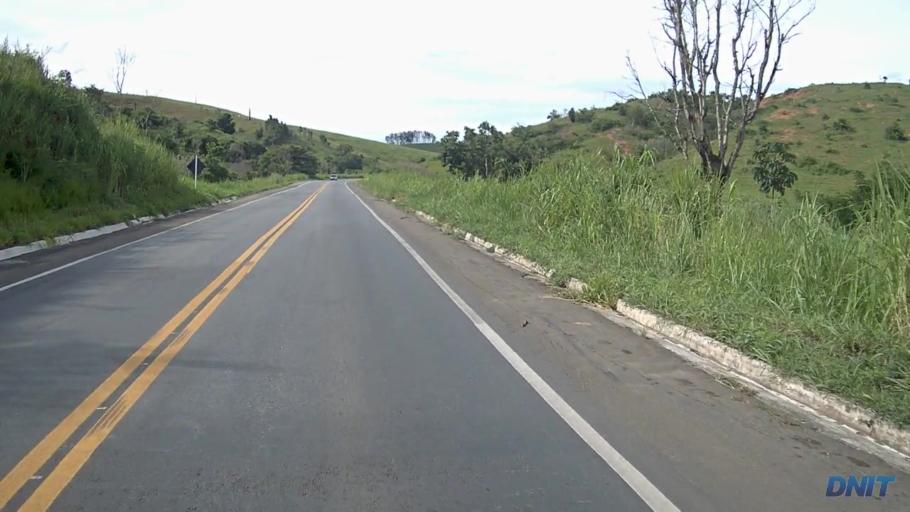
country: BR
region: Minas Gerais
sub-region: Belo Oriente
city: Belo Oriente
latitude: -19.2155
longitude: -42.3065
